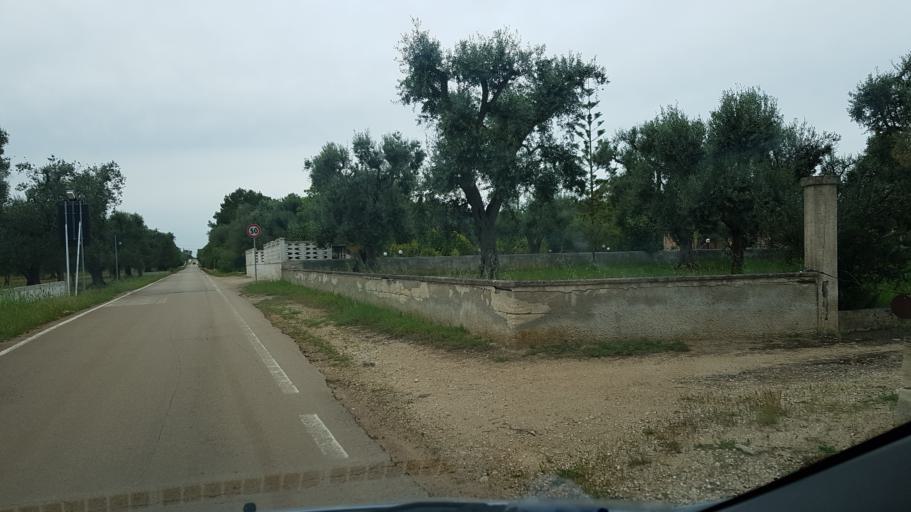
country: IT
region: Apulia
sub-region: Provincia di Brindisi
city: San Vito dei Normanni
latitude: 40.6676
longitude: 17.7651
